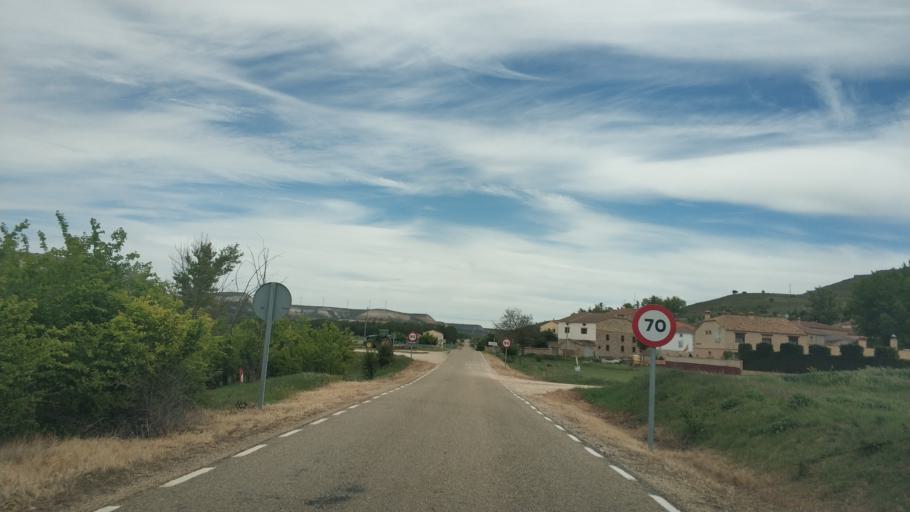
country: ES
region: Castille and Leon
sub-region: Provincia de Soria
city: Caltojar
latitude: 41.4314
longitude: -2.7973
